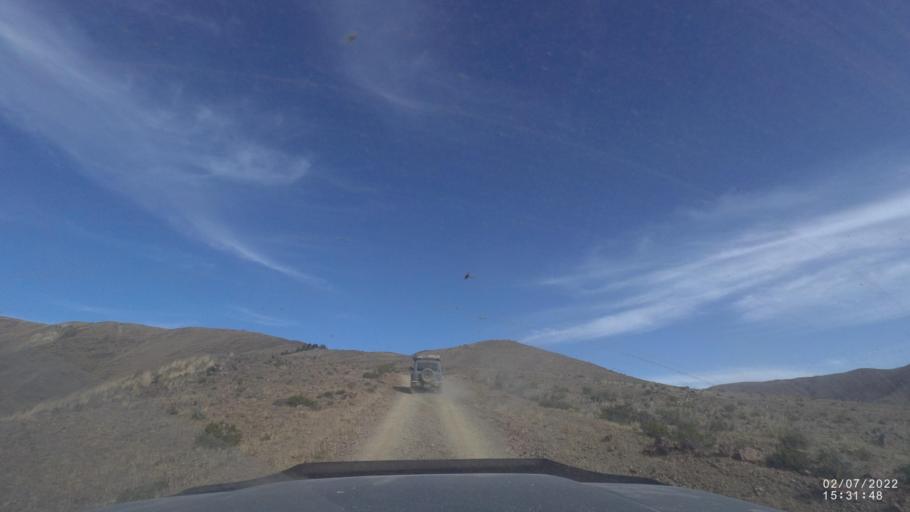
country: BO
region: Cochabamba
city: Irpa Irpa
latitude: -17.8830
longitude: -66.4146
